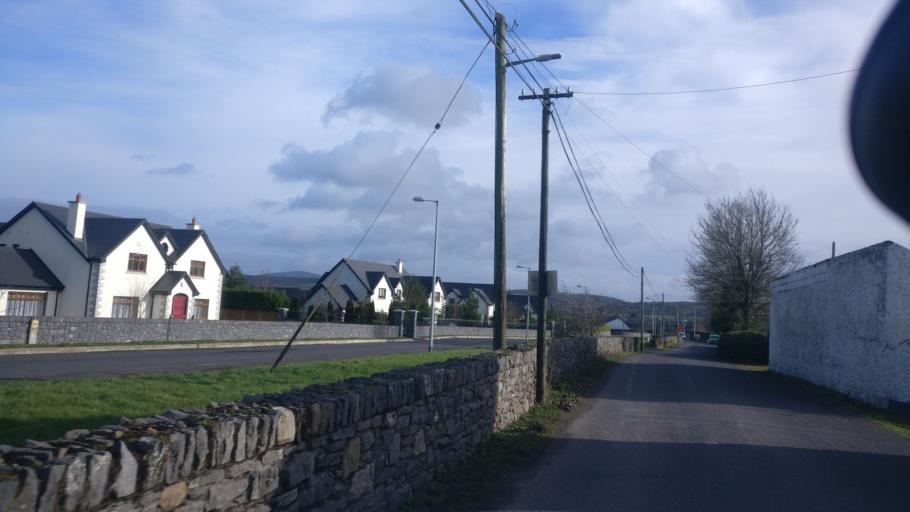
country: IE
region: Leinster
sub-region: Kilkenny
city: Thomastown
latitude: 52.5247
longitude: -7.1594
